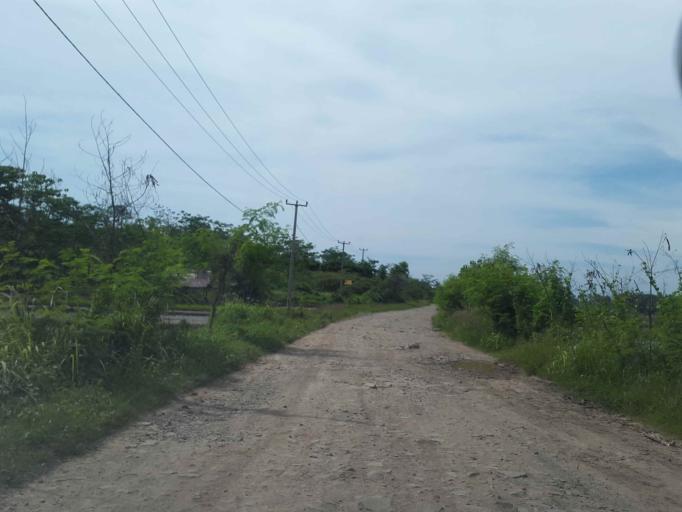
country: ID
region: Banten
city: Citeureup
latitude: -6.5024
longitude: 105.6677
